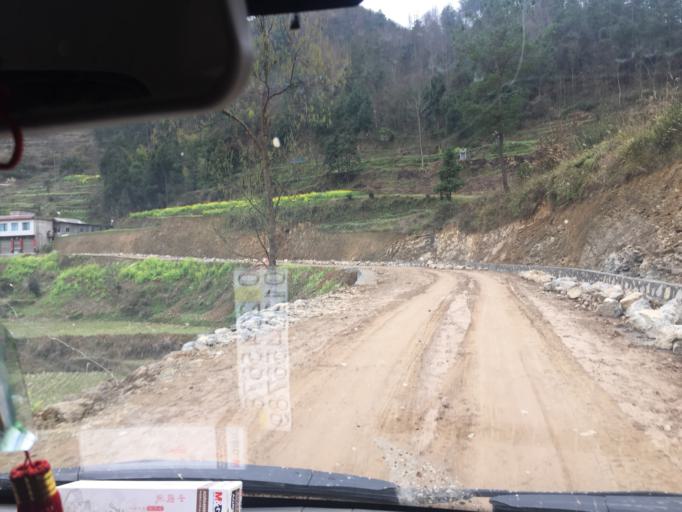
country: CN
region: Guizhou Sheng
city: Fuxing
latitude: 28.0693
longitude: 107.9122
